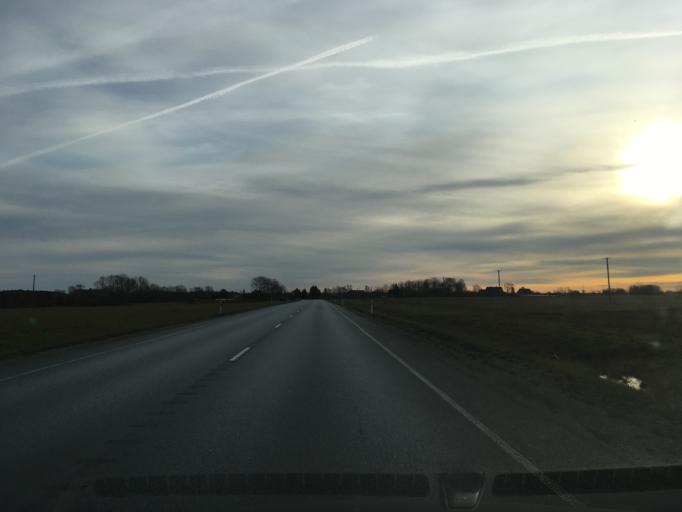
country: EE
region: Ida-Virumaa
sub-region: Kivioli linn
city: Kivioli
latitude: 59.4134
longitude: 26.9867
